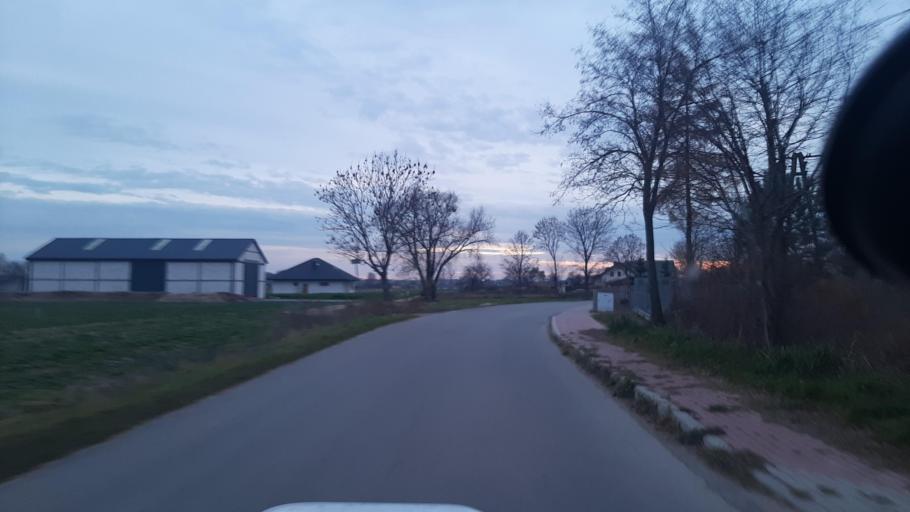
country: PL
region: Lublin Voivodeship
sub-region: Powiat lubelski
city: Garbow
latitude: 51.3661
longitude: 22.3841
